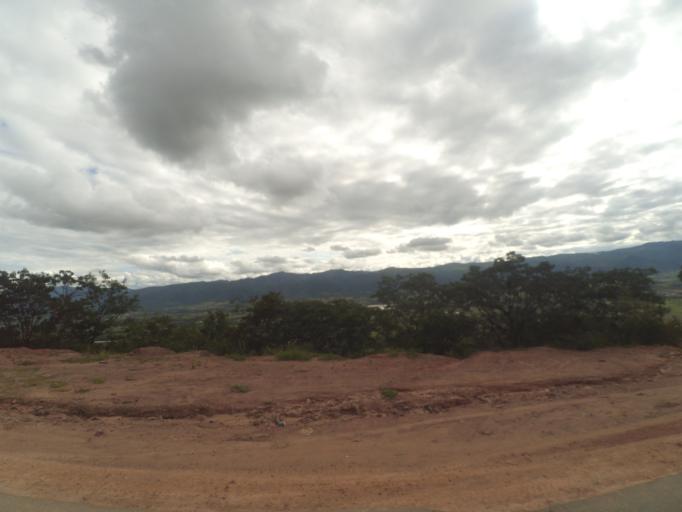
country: BO
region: Santa Cruz
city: Samaipata
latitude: -18.1660
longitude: -63.8919
